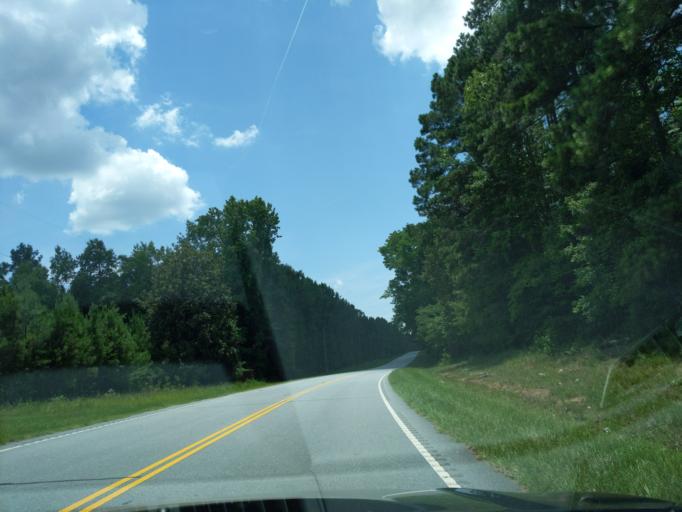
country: US
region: South Carolina
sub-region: Greenwood County
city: Ninety Six
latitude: 34.0091
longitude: -82.0429
